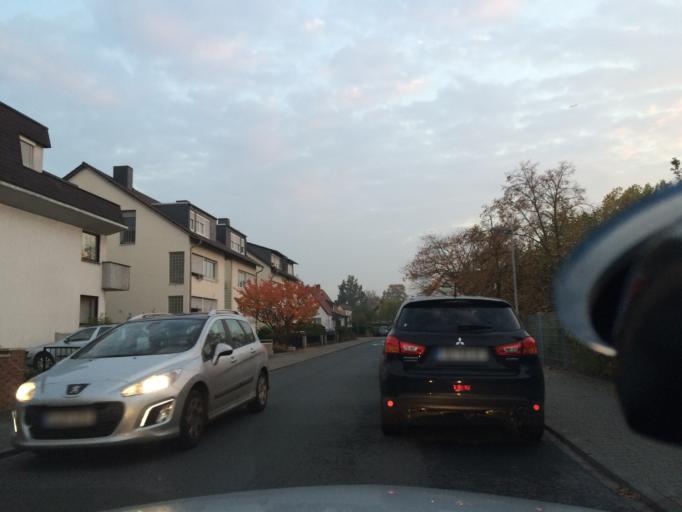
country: DE
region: Hesse
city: Morfelden-Walldorf
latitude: 49.9759
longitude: 8.5520
